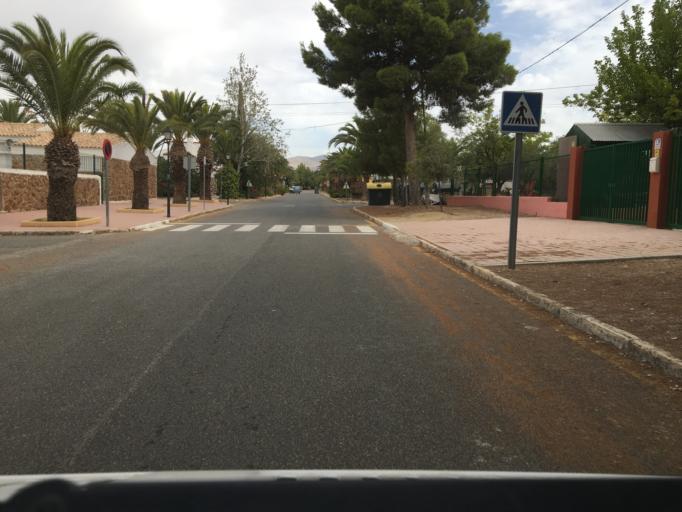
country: ES
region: Andalusia
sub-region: Provincia de Almeria
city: Huercal-Overa
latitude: 37.4198
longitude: -1.8776
